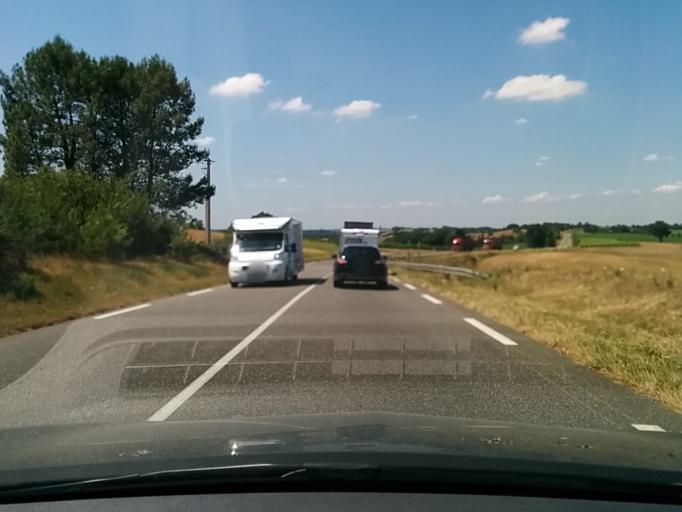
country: FR
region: Midi-Pyrenees
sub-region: Departement du Gers
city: Eauze
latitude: 43.7797
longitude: 0.1195
